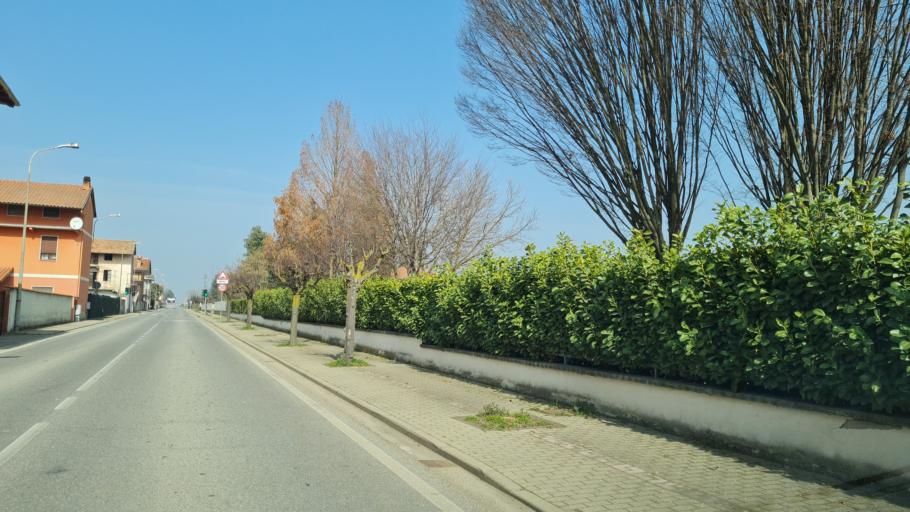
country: IT
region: Piedmont
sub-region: Provincia di Novara
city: Landiona
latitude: 45.5001
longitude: 8.4225
